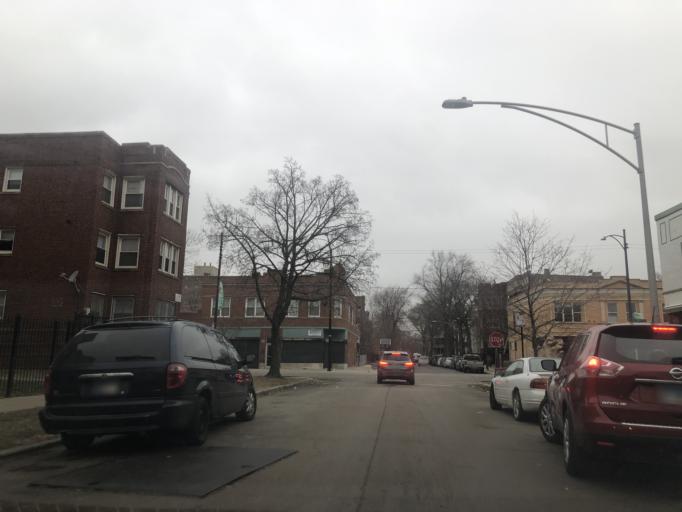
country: US
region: Illinois
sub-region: Cook County
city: Chicago
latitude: 41.7835
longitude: -87.6133
